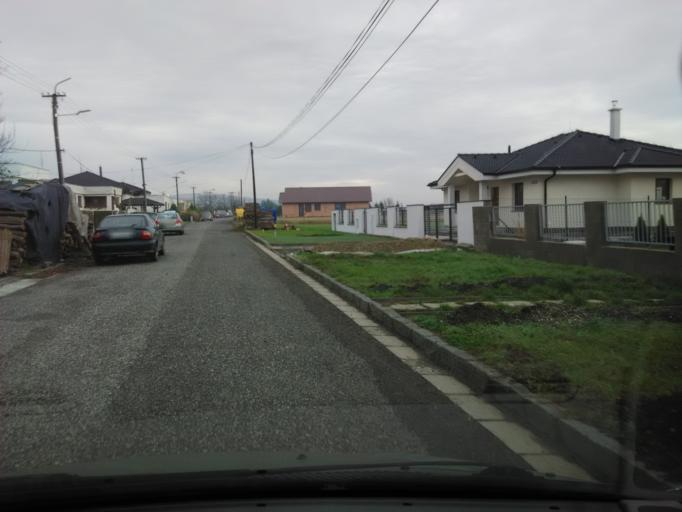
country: SK
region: Nitriansky
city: Tlmace
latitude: 48.2869
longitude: 18.5600
